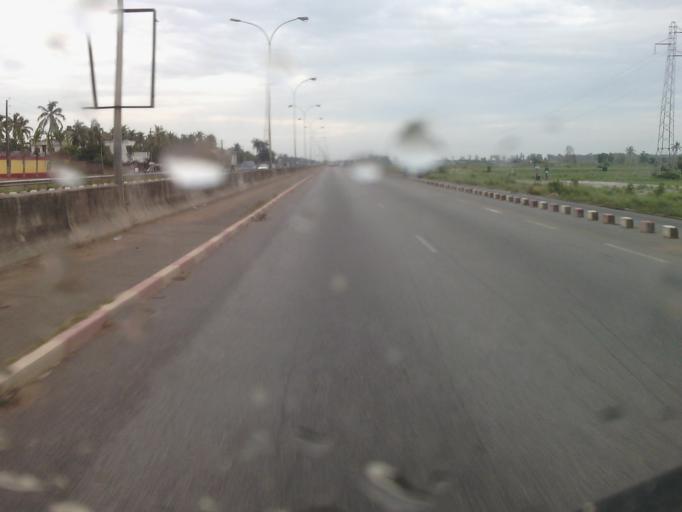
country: BJ
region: Queme
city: Porto-Novo
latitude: 6.3754
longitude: 2.5716
